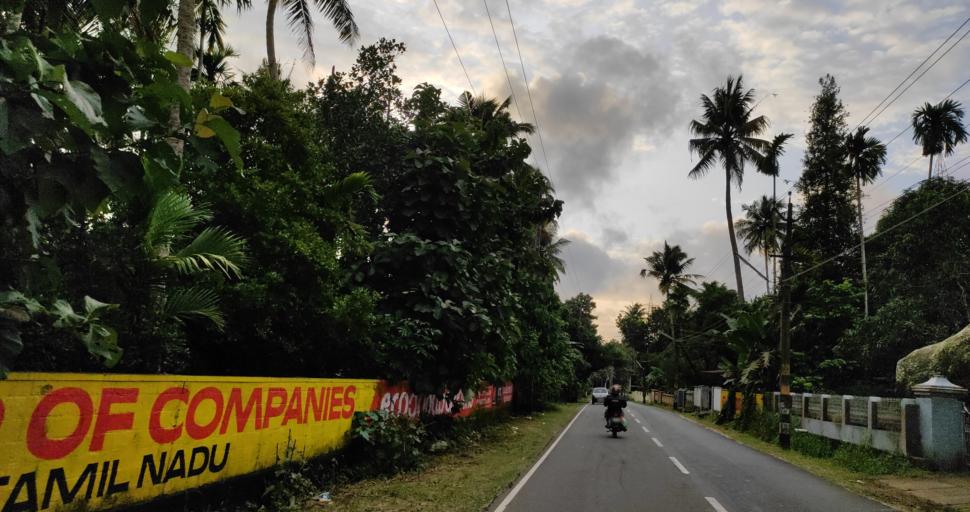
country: IN
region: Kerala
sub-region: Thrissur District
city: Kizhake Chalakudi
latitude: 10.3172
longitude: 76.3854
